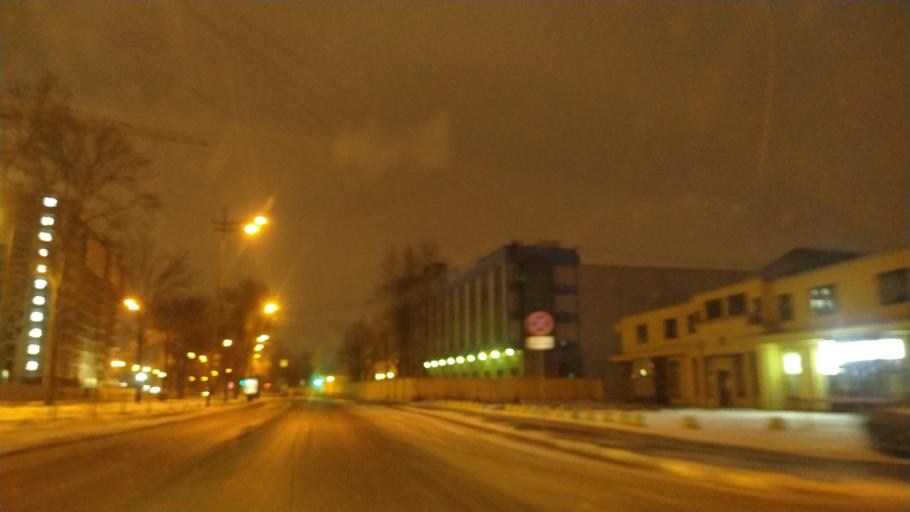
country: RU
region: St.-Petersburg
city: Centralniy
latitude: 59.8953
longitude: 30.3319
